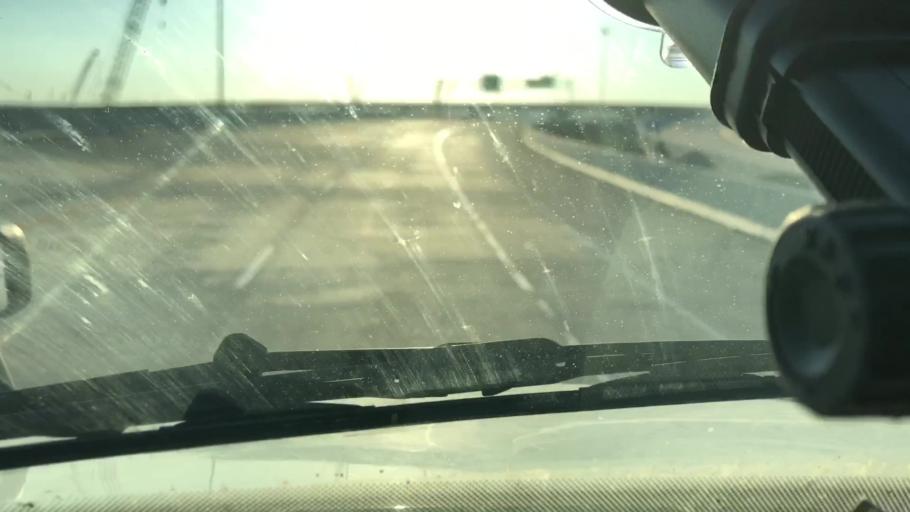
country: US
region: Iowa
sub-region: Pottawattamie County
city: Council Bluffs
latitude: 41.2321
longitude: -95.8351
